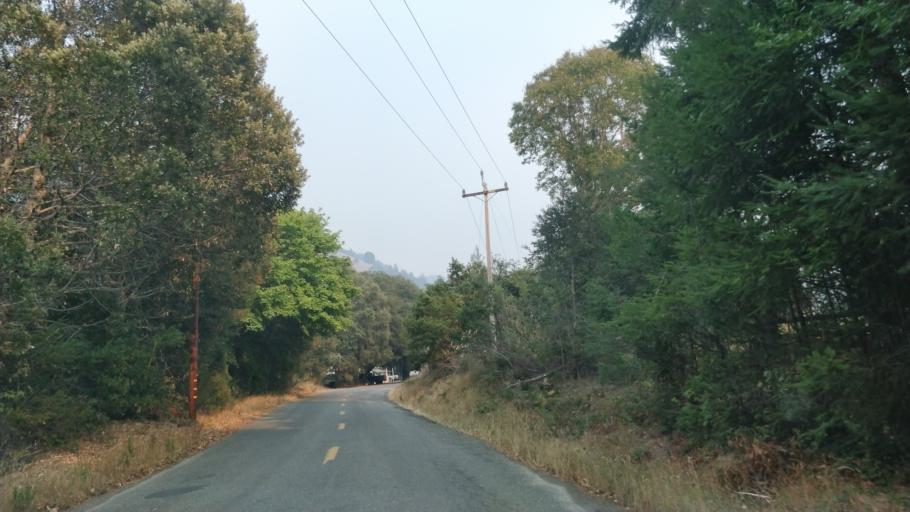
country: US
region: California
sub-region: Humboldt County
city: Rio Dell
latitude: 40.2432
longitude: -124.1257
